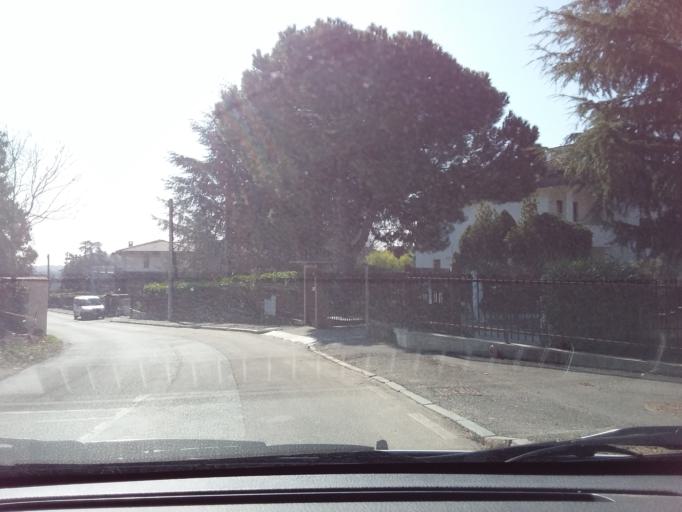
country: IT
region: Piedmont
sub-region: Provincia di Torino
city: Rivoli
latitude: 45.0802
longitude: 7.5246
